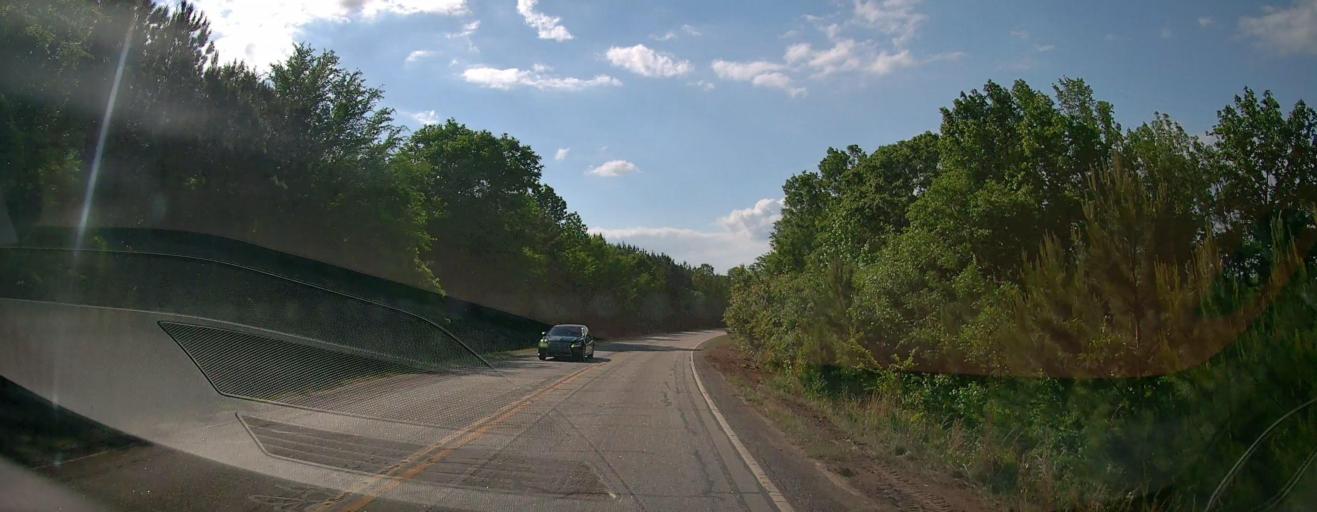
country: US
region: Georgia
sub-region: Washington County
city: Tennille
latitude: 32.9275
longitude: -83.0105
